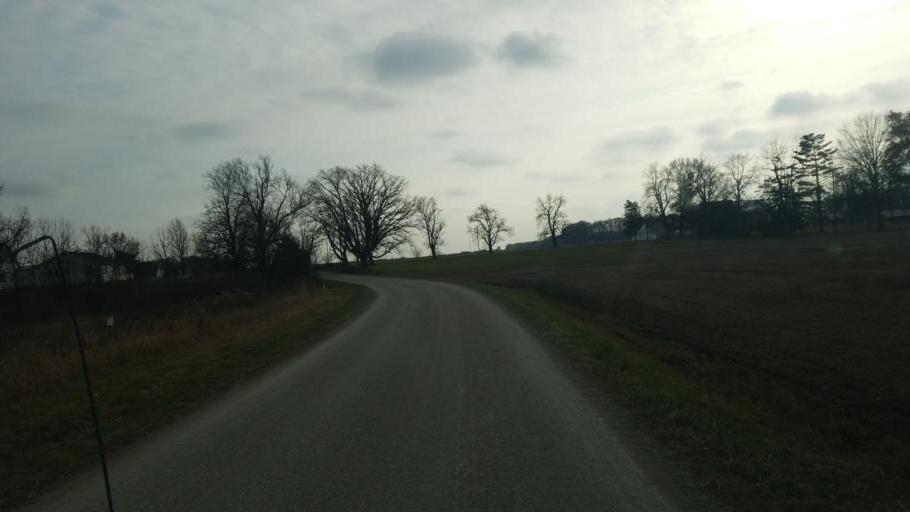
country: US
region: Indiana
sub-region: Adams County
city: Geneva
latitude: 40.6110
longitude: -84.9679
